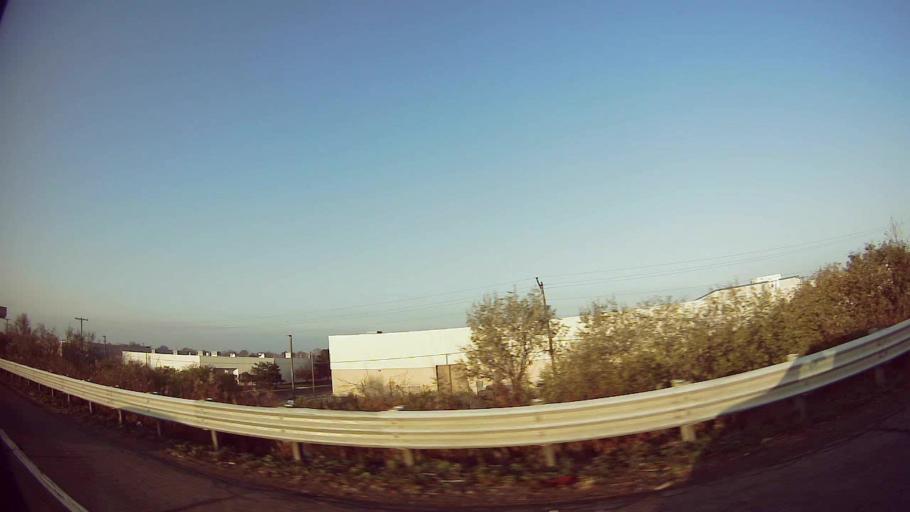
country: US
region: Michigan
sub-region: Oakland County
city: Clawson
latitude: 42.5185
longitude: -83.1156
